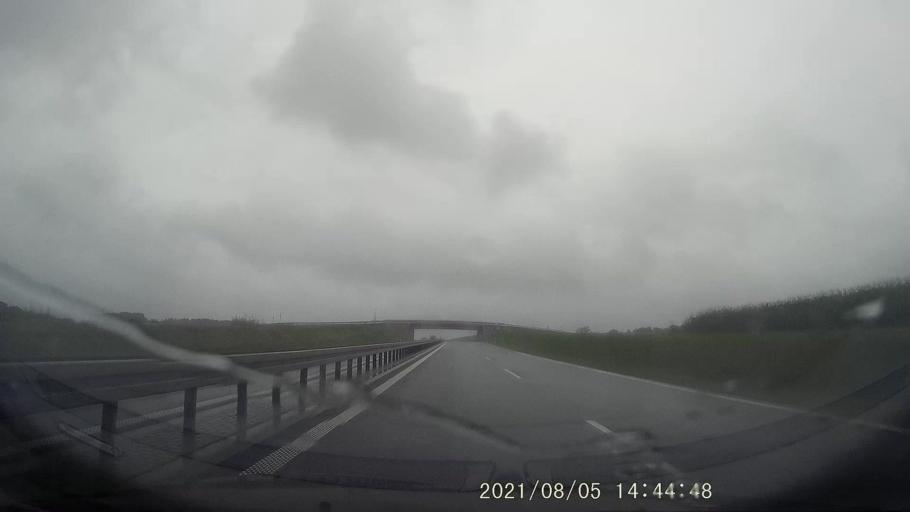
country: PL
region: Opole Voivodeship
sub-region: Powiat nyski
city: Nysa
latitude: 50.4964
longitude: 17.3714
